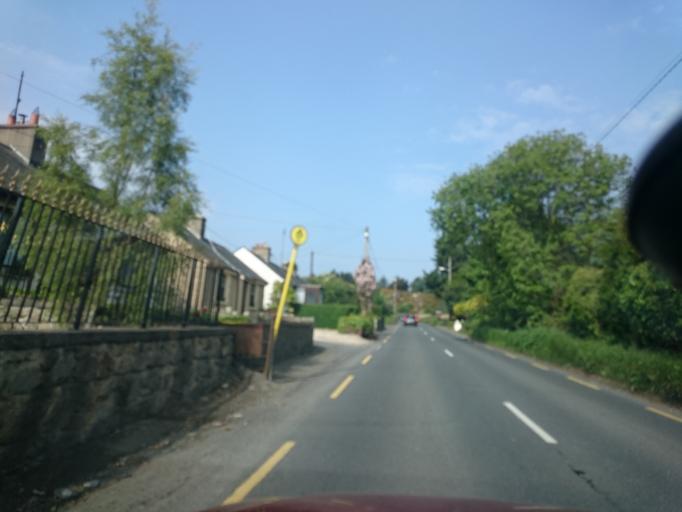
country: IE
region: Leinster
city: Balally
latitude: 53.2654
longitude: -6.2343
